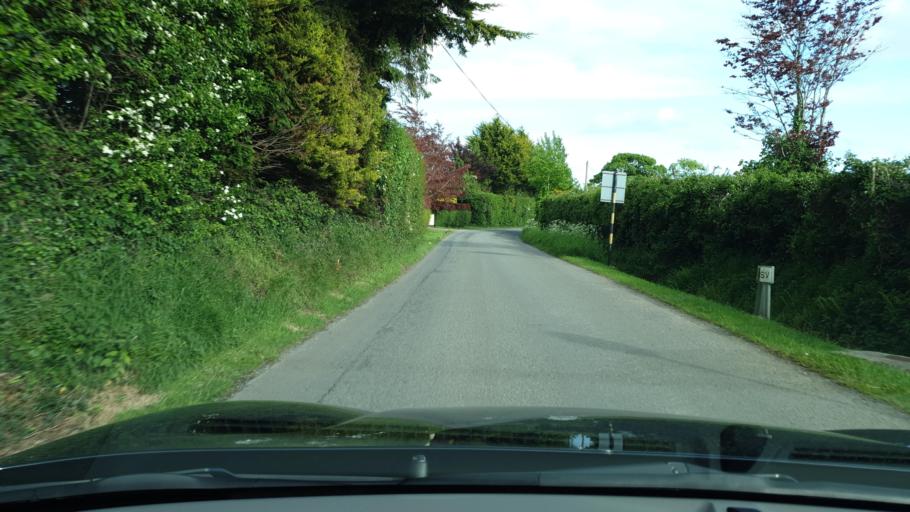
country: IE
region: Leinster
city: Balrothery
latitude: 53.5503
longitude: -6.2066
